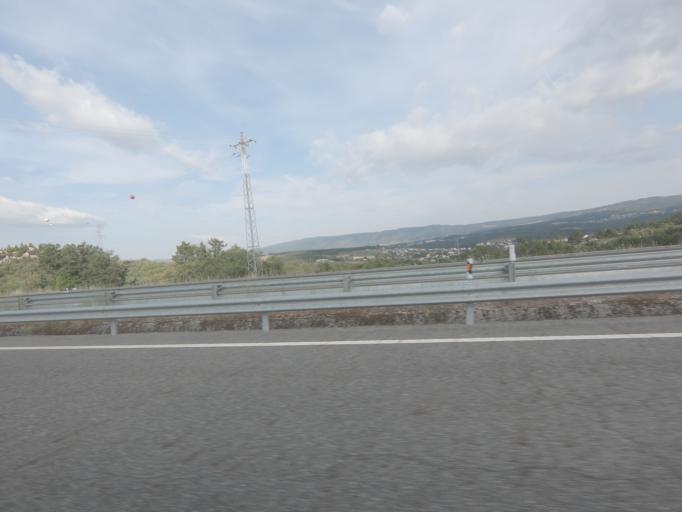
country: PT
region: Vila Real
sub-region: Chaves
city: Chaves
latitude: 41.7247
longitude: -7.5423
